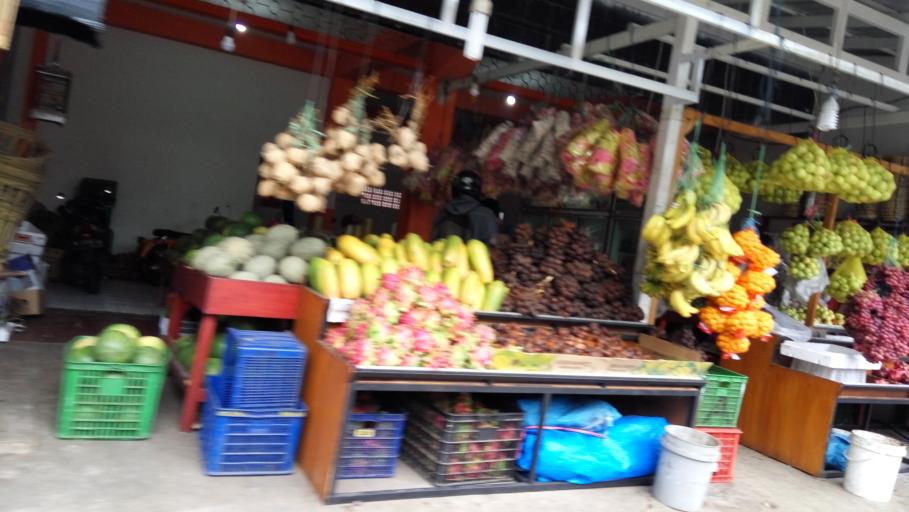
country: ID
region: East Java
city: Malang
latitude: -7.9353
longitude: 112.6048
